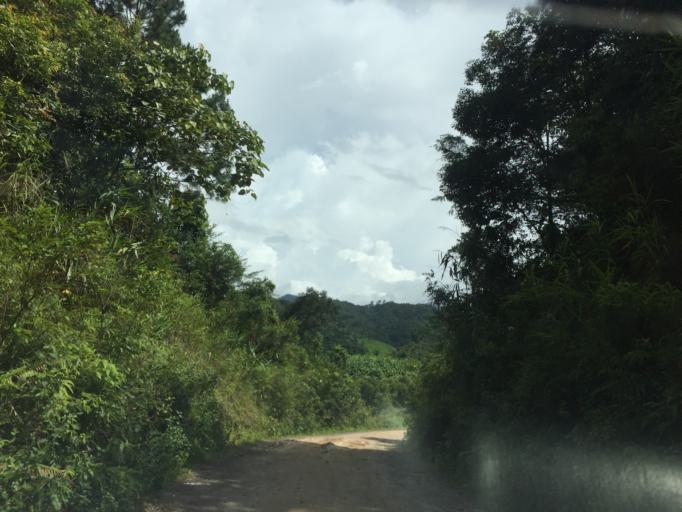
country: LA
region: Xiangkhoang
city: Muang Phonsavan
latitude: 19.3377
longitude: 103.5169
